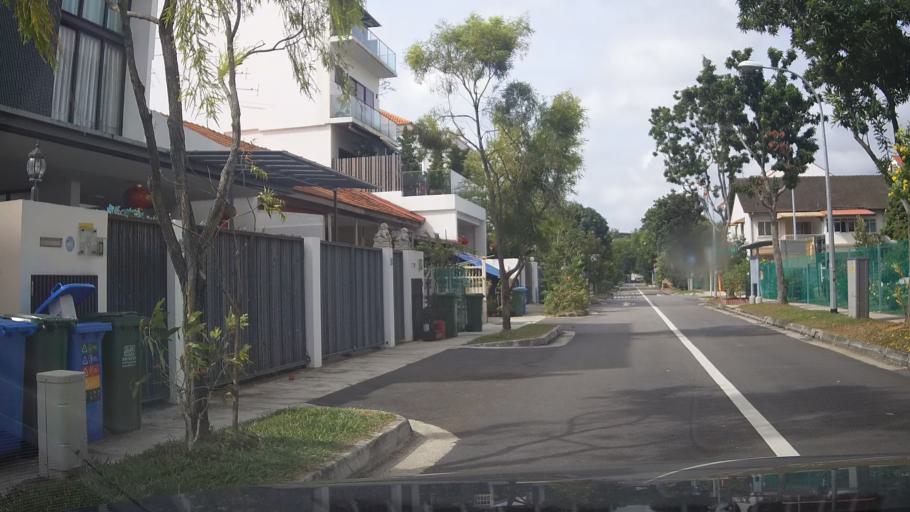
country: SG
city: Singapore
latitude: 1.3069
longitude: 103.9032
